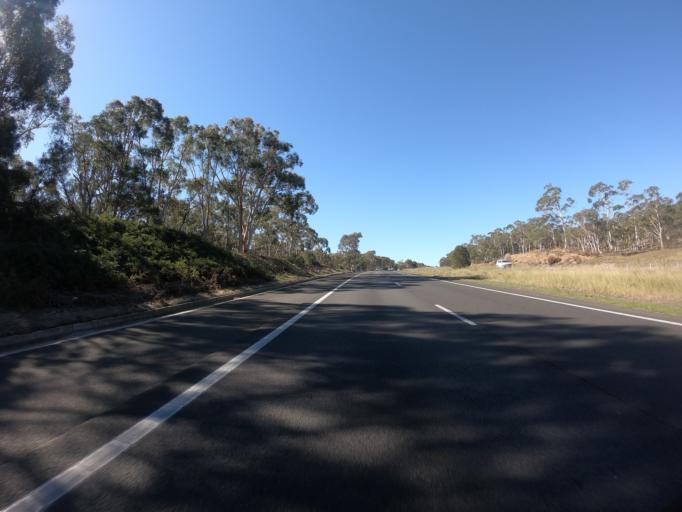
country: AU
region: New South Wales
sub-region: Wingecarribee
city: Bundanoon
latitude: -34.6508
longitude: 150.0921
